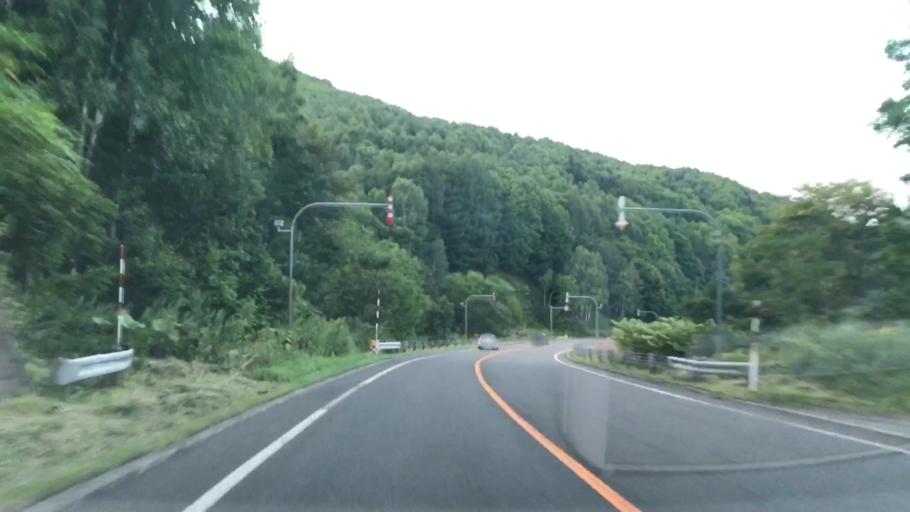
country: JP
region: Hokkaido
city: Sapporo
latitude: 42.9100
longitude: 141.1199
